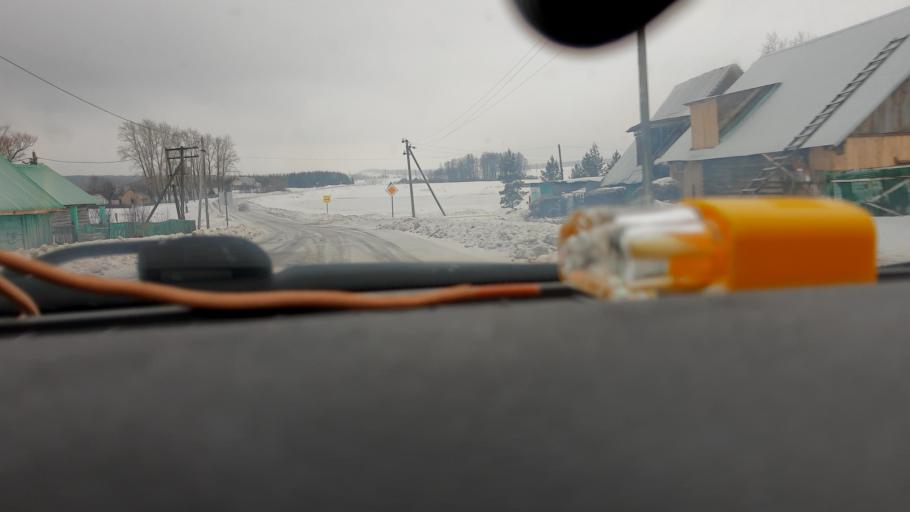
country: RU
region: Bashkortostan
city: Ulukulevo
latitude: 54.6074
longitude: 56.4261
